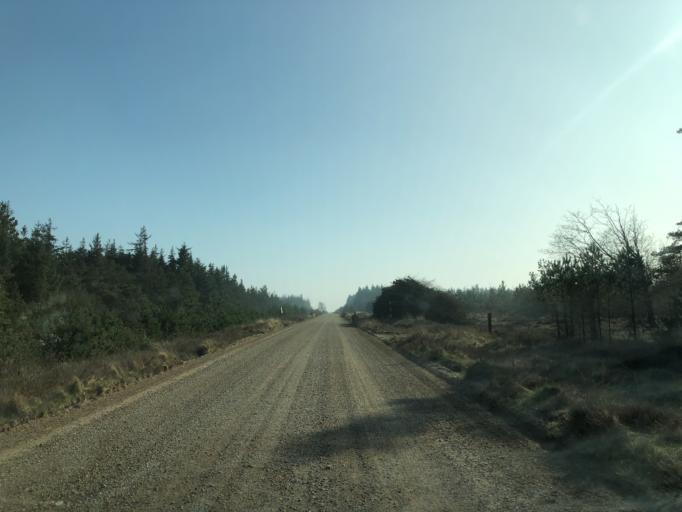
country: DK
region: South Denmark
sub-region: Varde Kommune
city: Oksbol
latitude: 55.6108
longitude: 8.1639
